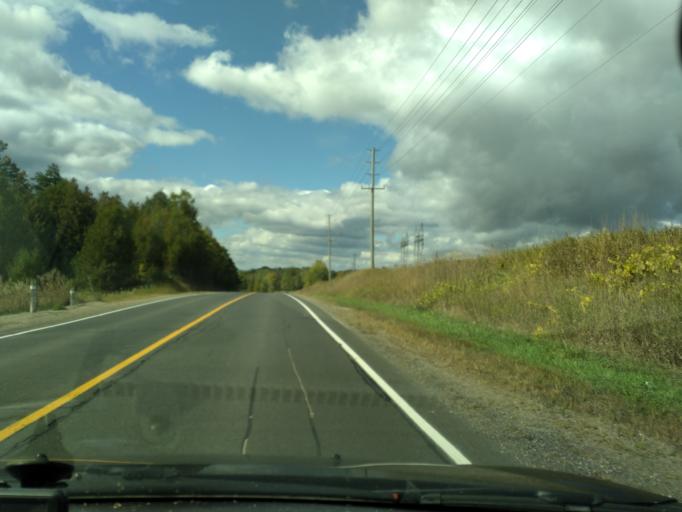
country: CA
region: Ontario
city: Angus
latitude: 44.2598
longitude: -79.7721
